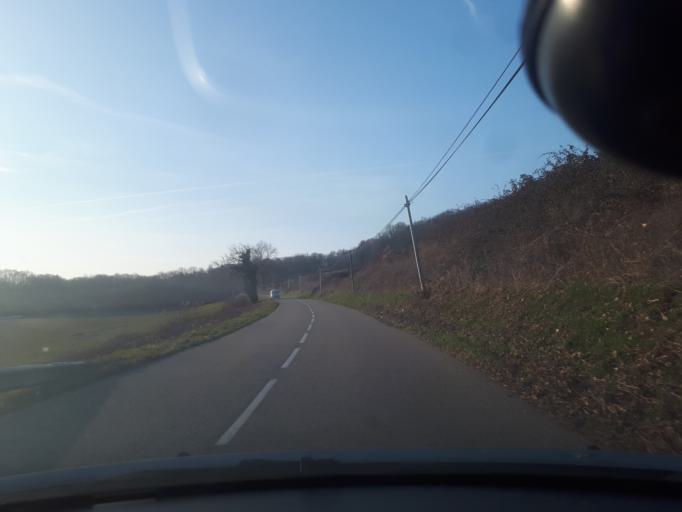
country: FR
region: Rhone-Alpes
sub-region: Departement de l'Isere
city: Morestel
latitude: 45.6675
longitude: 5.4411
